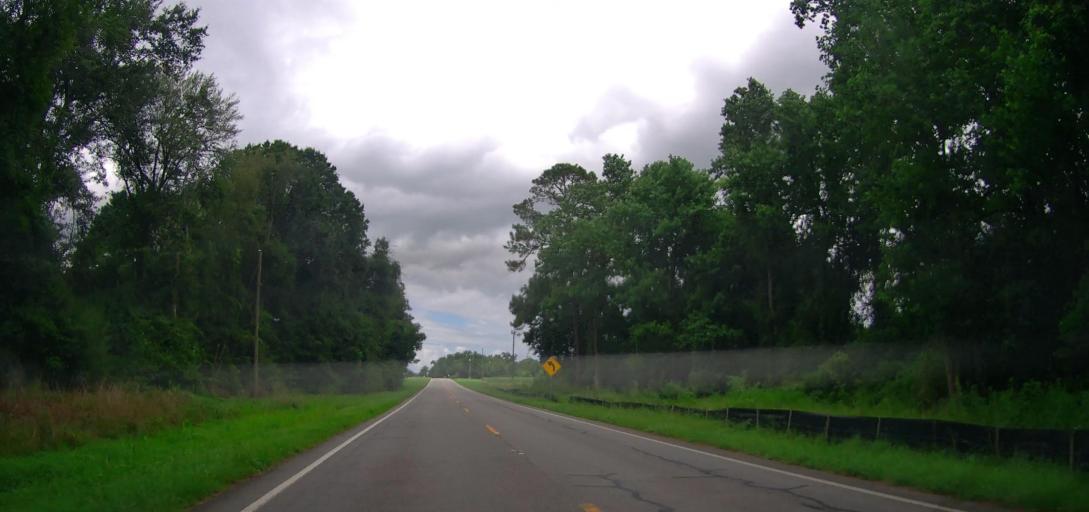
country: US
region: Georgia
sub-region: Wilcox County
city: Rochelle
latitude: 31.9519
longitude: -83.5407
